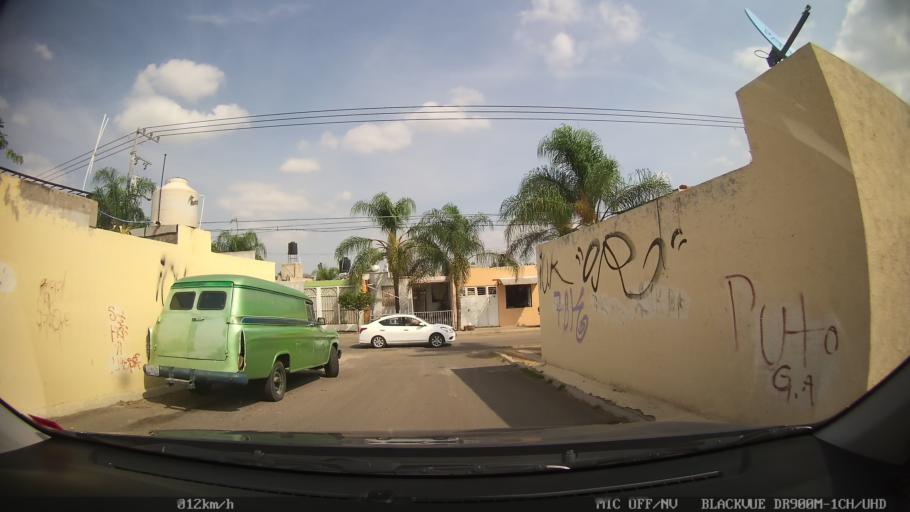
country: MX
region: Jalisco
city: Coyula
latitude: 20.6524
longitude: -103.2128
